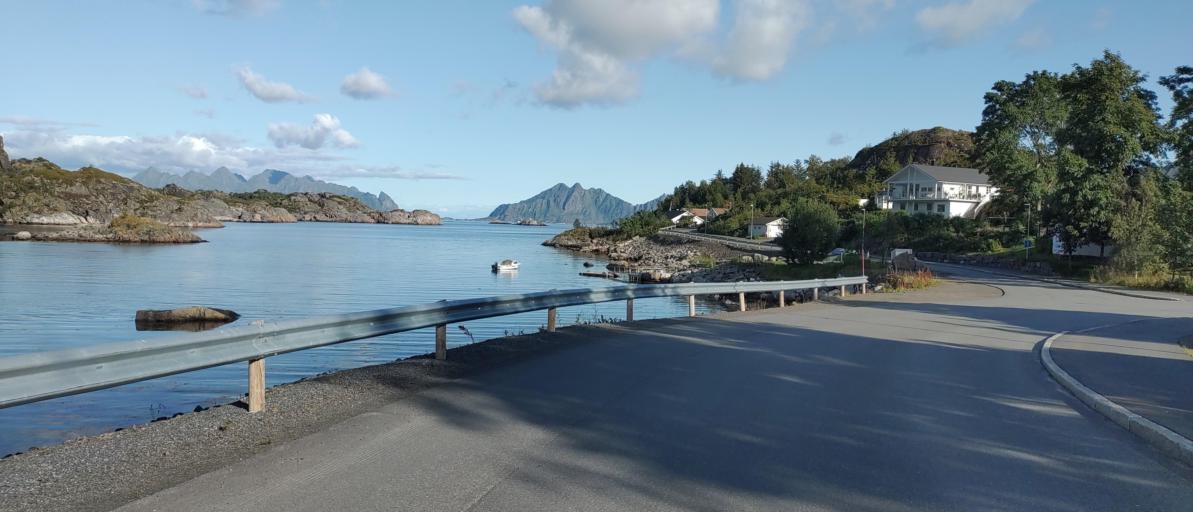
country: NO
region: Nordland
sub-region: Vagan
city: Kabelvag
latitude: 68.2146
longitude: 14.4853
